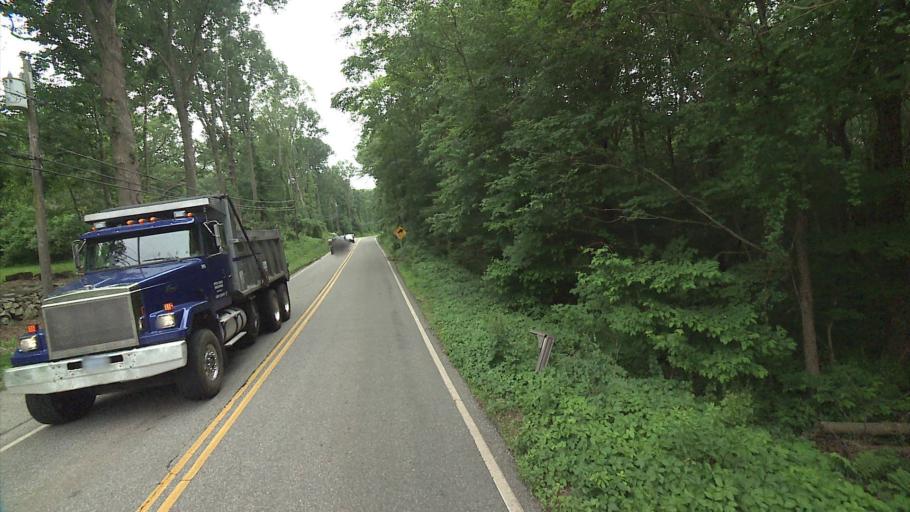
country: US
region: Connecticut
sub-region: Tolland County
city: Hebron
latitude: 41.6918
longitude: -72.3614
